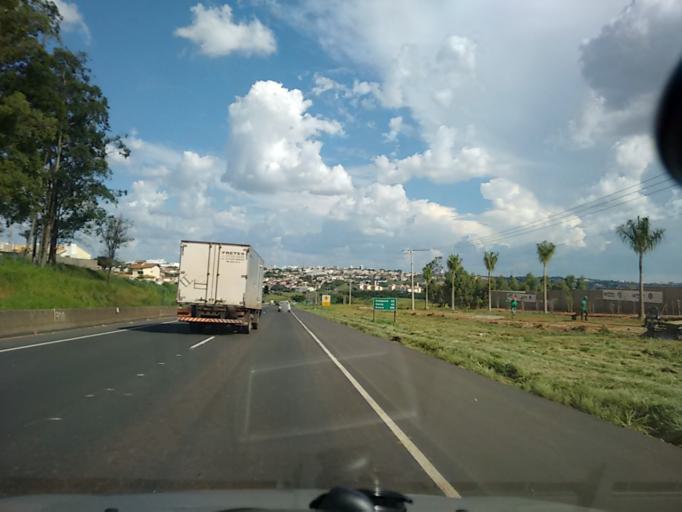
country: BR
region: Sao Paulo
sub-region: Marilia
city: Marilia
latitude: -22.1851
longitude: -49.9709
